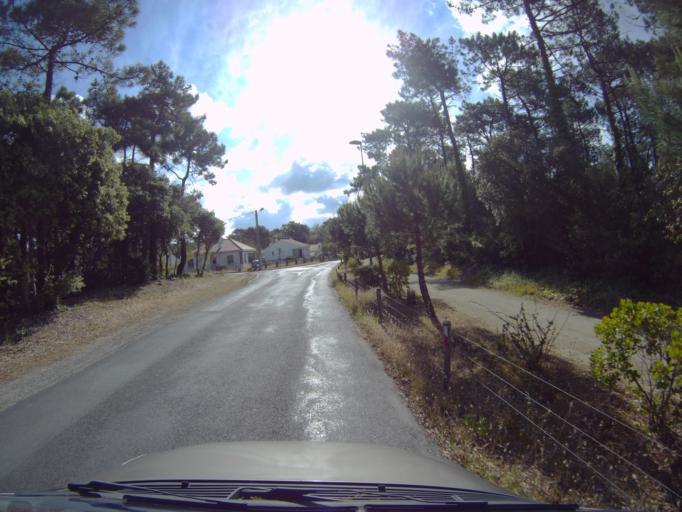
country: FR
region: Pays de la Loire
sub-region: Departement de la Vendee
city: La Barre-de-Monts
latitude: 46.8864
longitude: -2.1322
